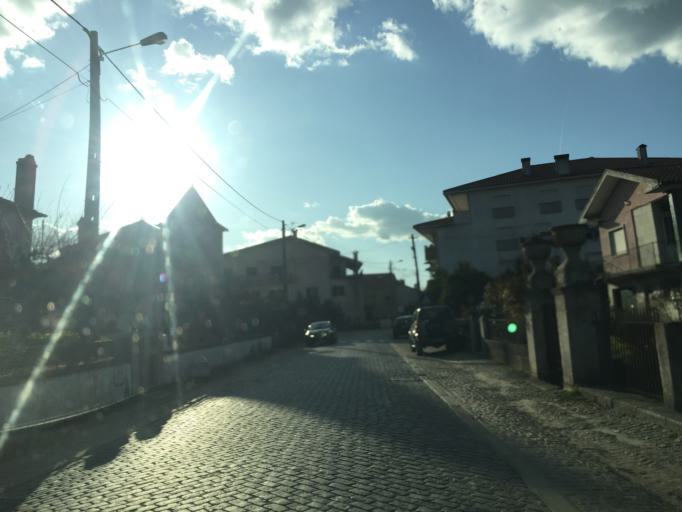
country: PT
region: Viseu
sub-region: Nelas
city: Nelas
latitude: 40.4772
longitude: -7.7841
